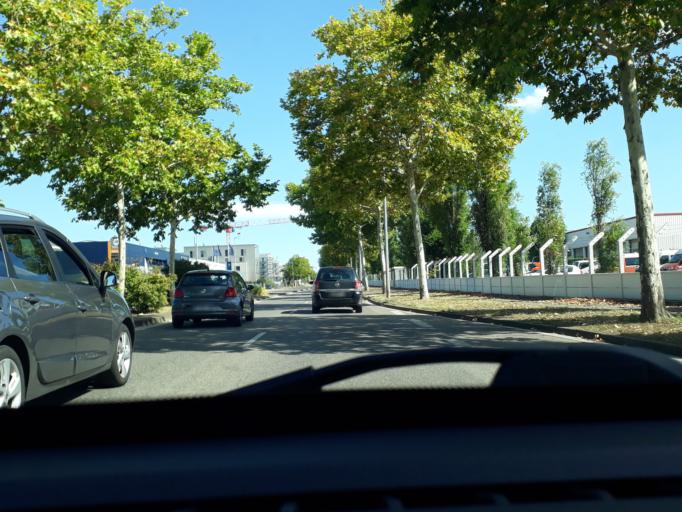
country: FR
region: Rhone-Alpes
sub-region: Departement du Rhone
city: Saint-Priest
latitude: 45.7013
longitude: 4.9180
